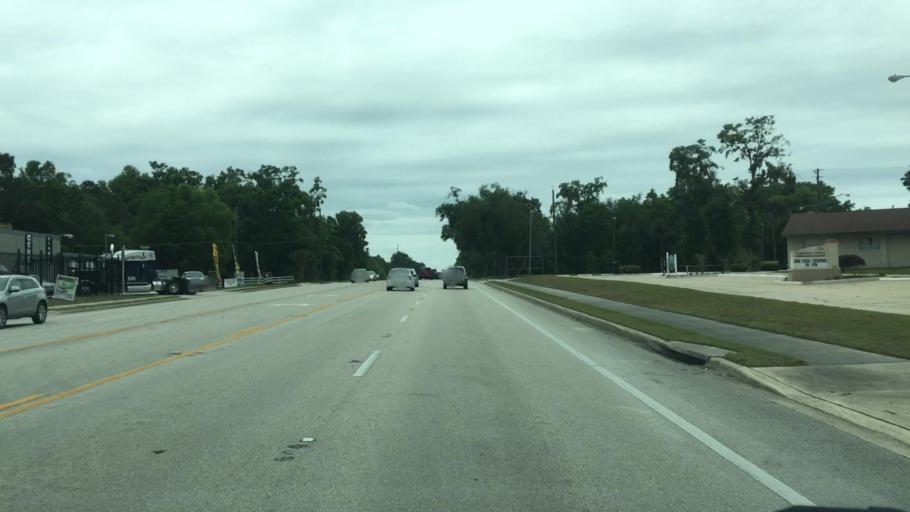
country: US
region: Florida
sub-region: Volusia County
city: De Land Southwest
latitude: 29.0017
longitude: -81.3143
